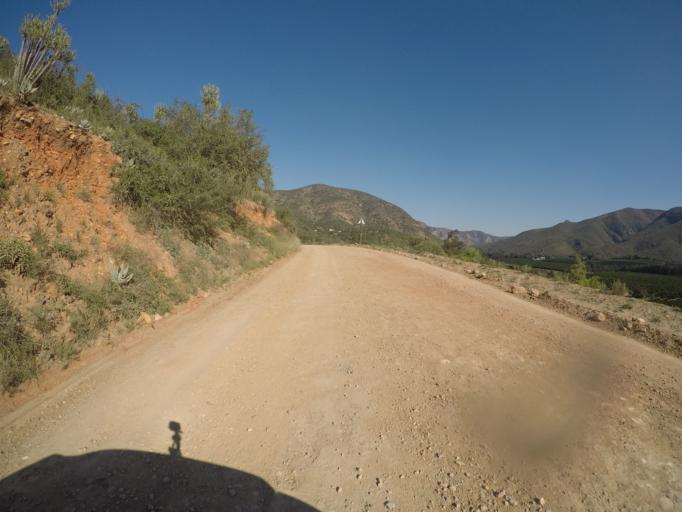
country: ZA
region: Eastern Cape
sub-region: Cacadu District Municipality
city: Kruisfontein
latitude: -33.6642
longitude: 24.5666
